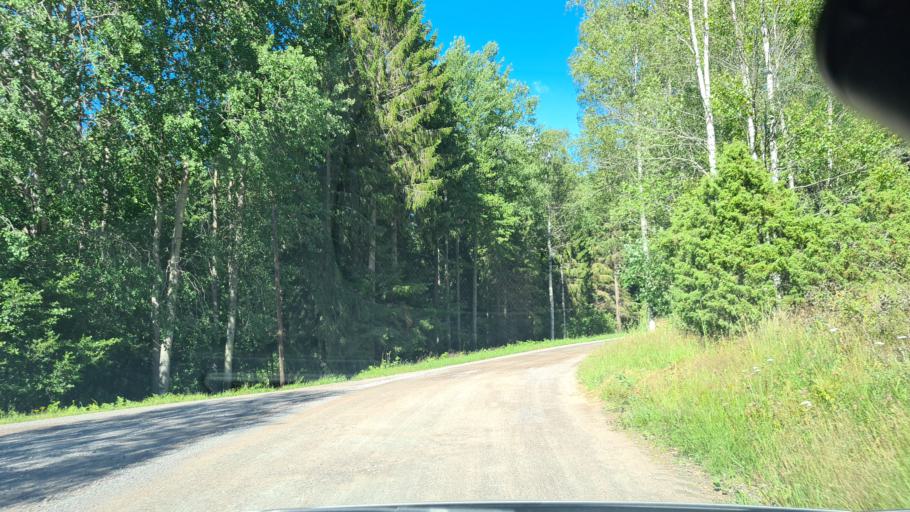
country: SE
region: OEstergoetland
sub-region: Norrkopings Kommun
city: Krokek
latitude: 58.6799
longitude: 16.4297
